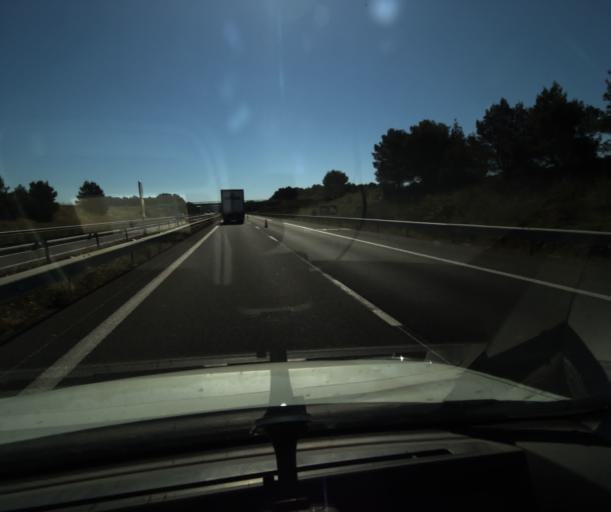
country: FR
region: Languedoc-Roussillon
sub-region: Departement de l'Aude
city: Ferrals-les-Corbieres
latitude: 43.1678
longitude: 2.7185
